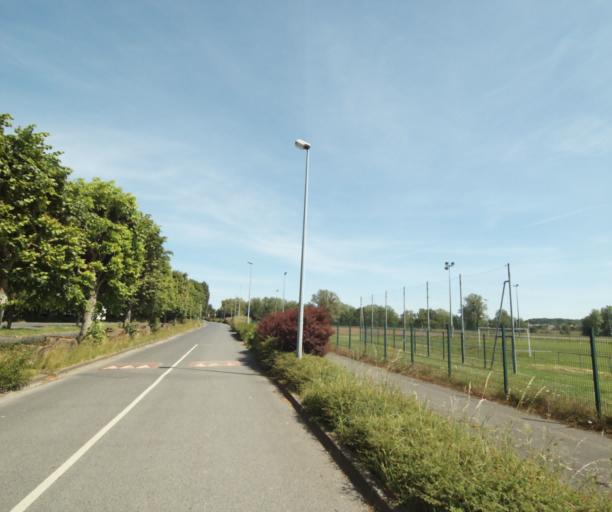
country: FR
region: Champagne-Ardenne
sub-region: Departement des Ardennes
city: Prix-les-Mezieres
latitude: 49.7602
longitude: 4.6887
